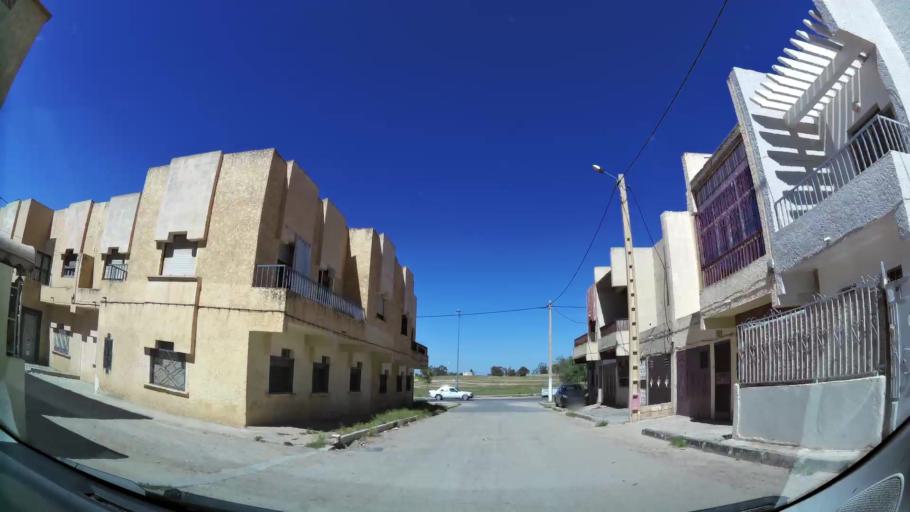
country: MA
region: Oriental
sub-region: Oujda-Angad
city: Oujda
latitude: 34.6640
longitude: -1.8685
